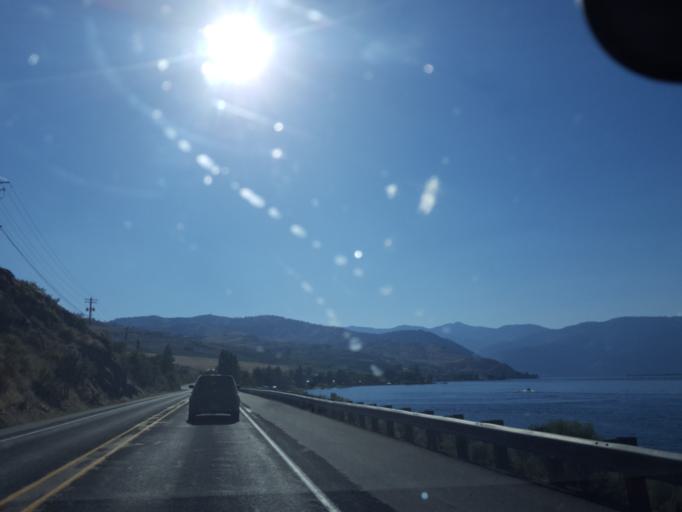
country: US
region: Washington
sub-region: Chelan County
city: Chelan
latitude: 47.8360
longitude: -120.0653
